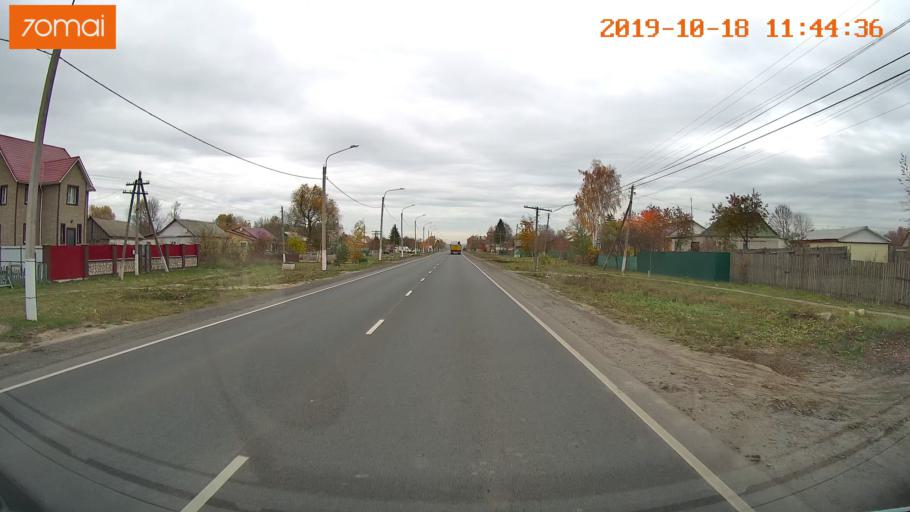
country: RU
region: Rjazan
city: Oktyabr'skiy
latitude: 54.2036
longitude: 38.9601
